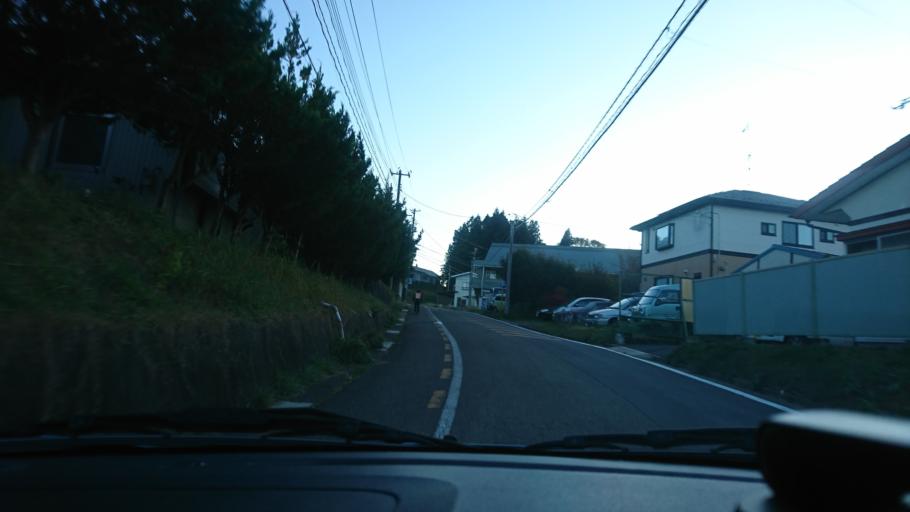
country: JP
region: Iwate
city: Ichinoseki
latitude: 38.8650
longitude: 141.3517
